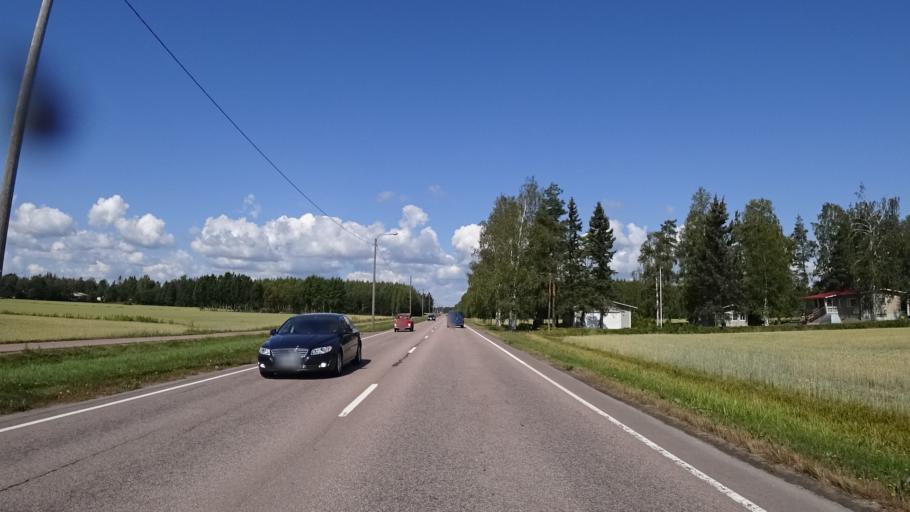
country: FI
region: Kymenlaakso
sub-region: Kotka-Hamina
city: Karhula
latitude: 60.5291
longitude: 26.9404
